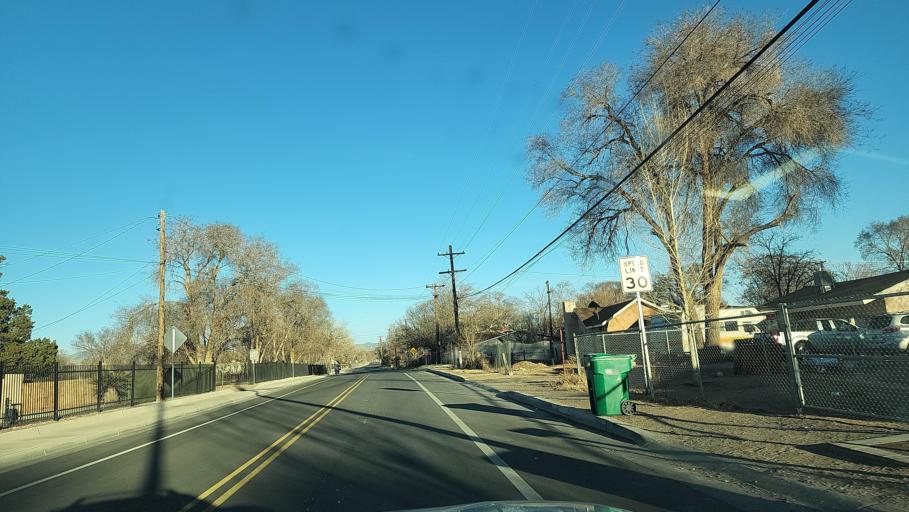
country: US
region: New Mexico
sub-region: Bernalillo County
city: South Valley
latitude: 35.0305
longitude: -106.6898
